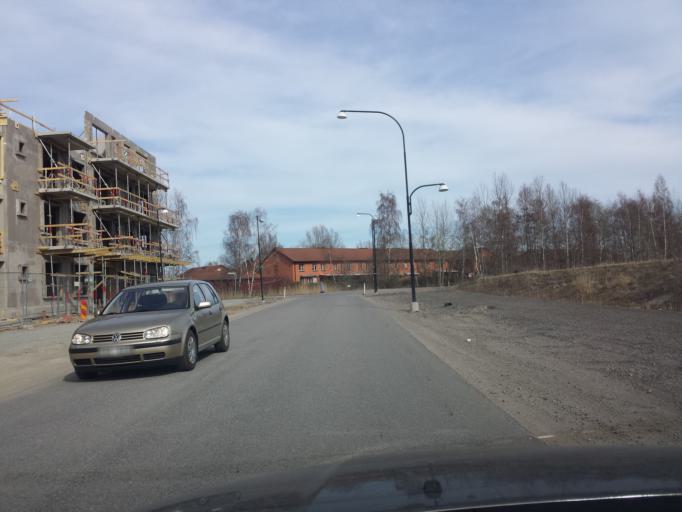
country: SE
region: OErebro
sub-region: Orebro Kommun
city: Orebro
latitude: 59.2520
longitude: 15.2228
